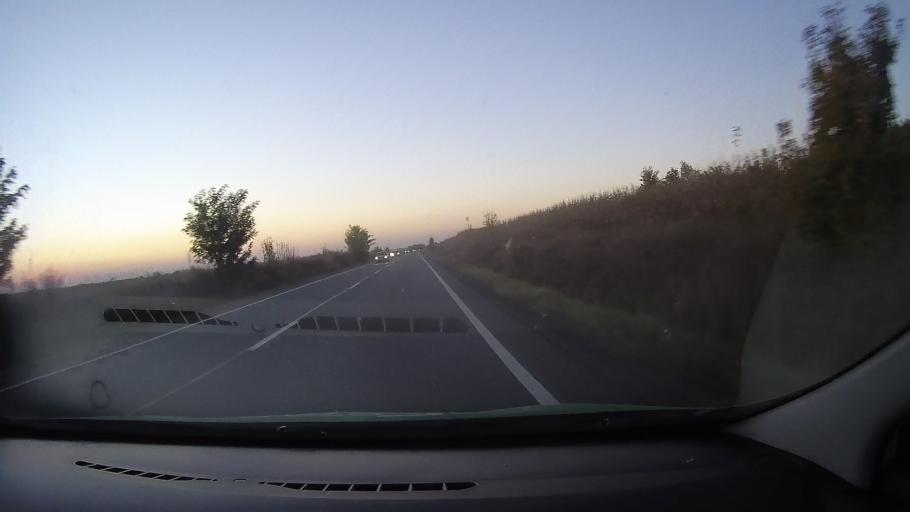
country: RO
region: Bihor
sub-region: Comuna Tarcea
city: Tarcea
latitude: 47.4364
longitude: 22.1999
